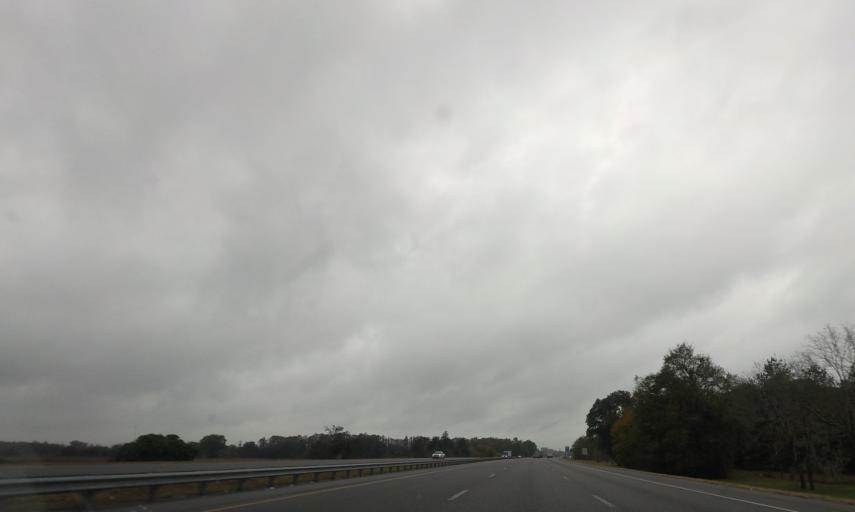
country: US
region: Georgia
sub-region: Echols County
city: Statenville
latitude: 30.6279
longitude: -83.1738
